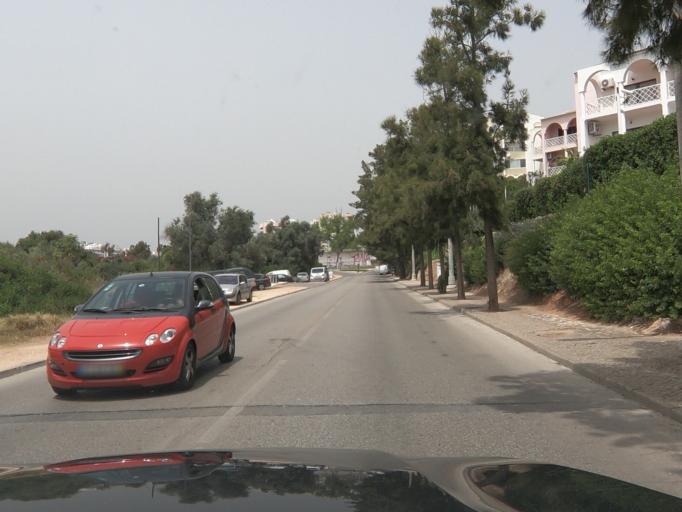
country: PT
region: Faro
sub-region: Portimao
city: Portimao
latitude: 37.1237
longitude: -8.5414
